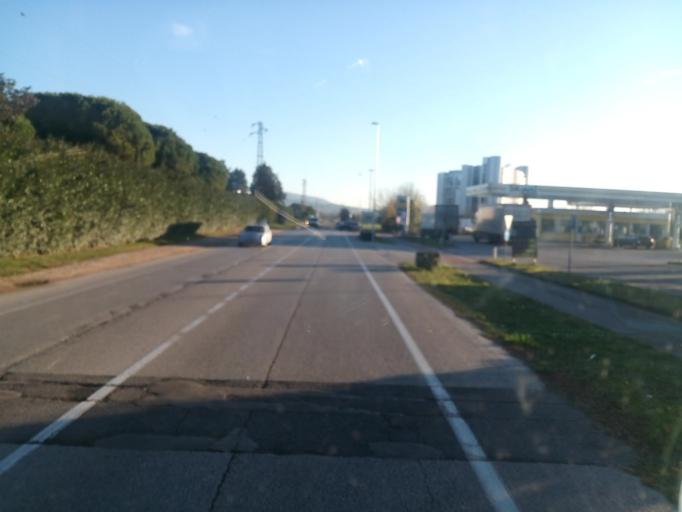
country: IT
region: Veneto
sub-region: Provincia di Vicenza
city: Santorso
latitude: 45.7176
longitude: 11.3911
